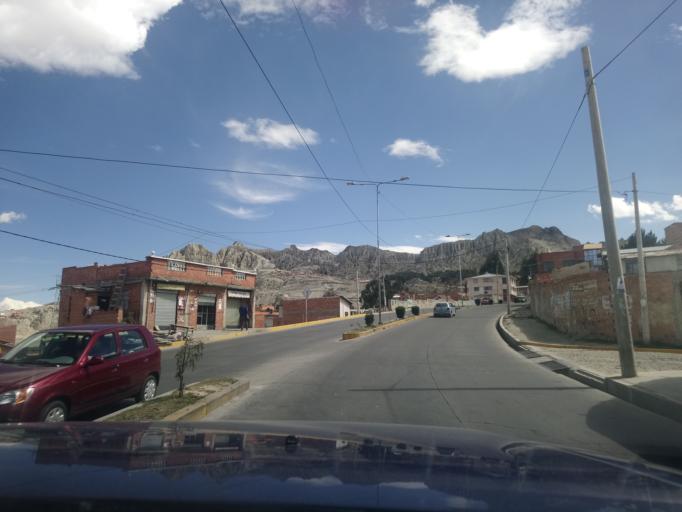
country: BO
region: La Paz
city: La Paz
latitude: -16.5283
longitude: -68.1252
